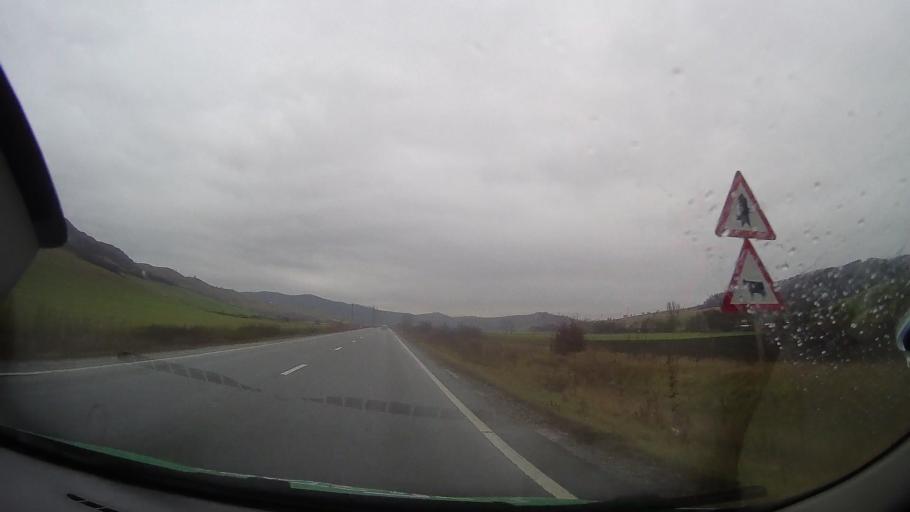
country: RO
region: Bistrita-Nasaud
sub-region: Comuna Teaca
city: Teaca
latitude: 46.9315
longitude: 24.4811
